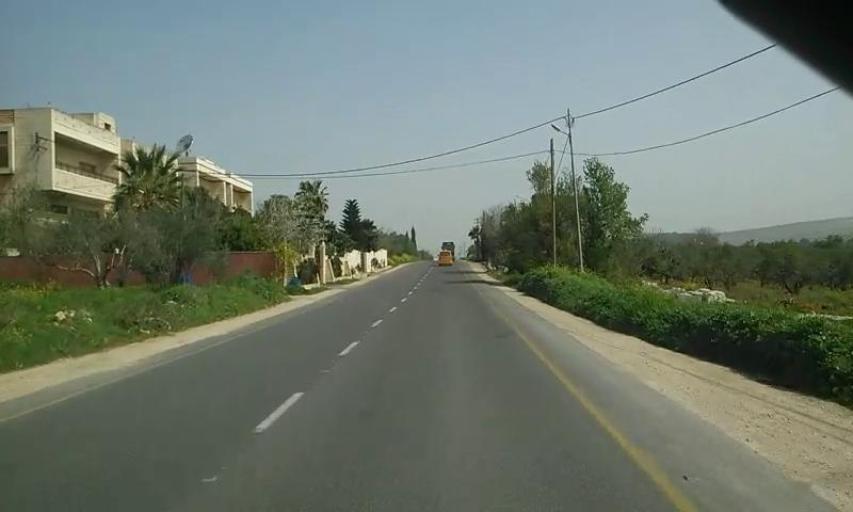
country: PS
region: West Bank
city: Udalah
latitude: 32.1690
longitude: 35.2672
